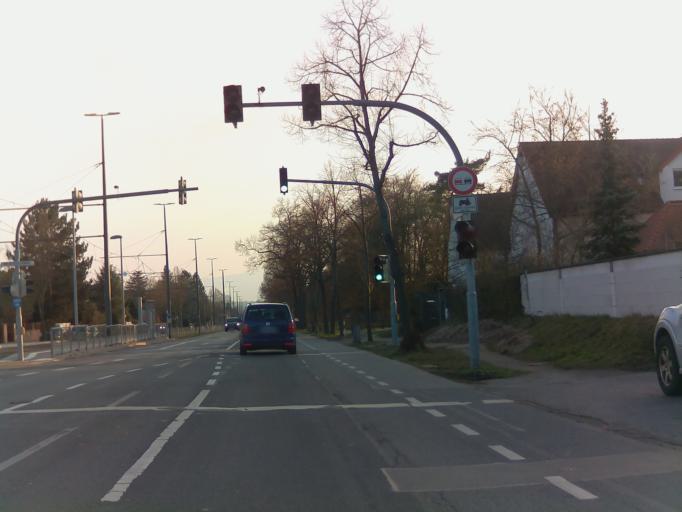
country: DE
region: Hesse
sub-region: Regierungsbezirk Darmstadt
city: Darmstadt
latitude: 49.8295
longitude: 8.6449
